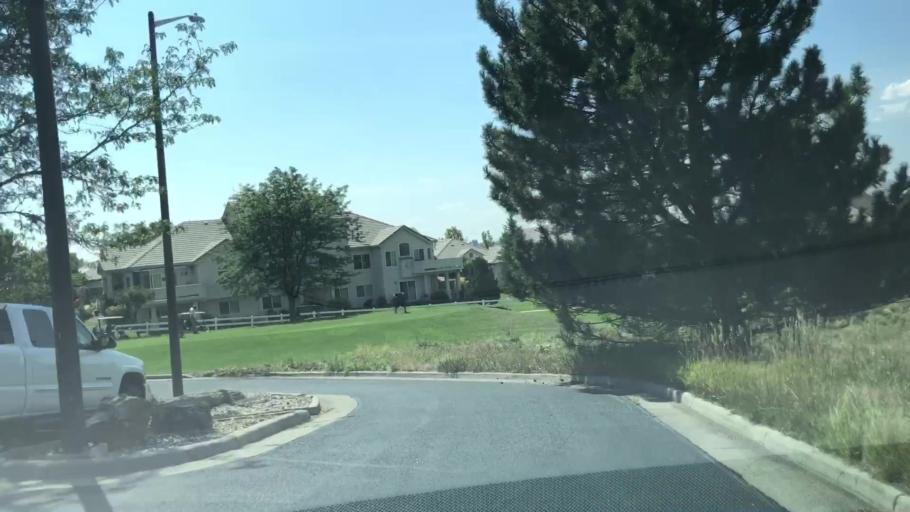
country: US
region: Colorado
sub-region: Larimer County
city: Loveland
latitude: 40.3985
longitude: -105.1430
